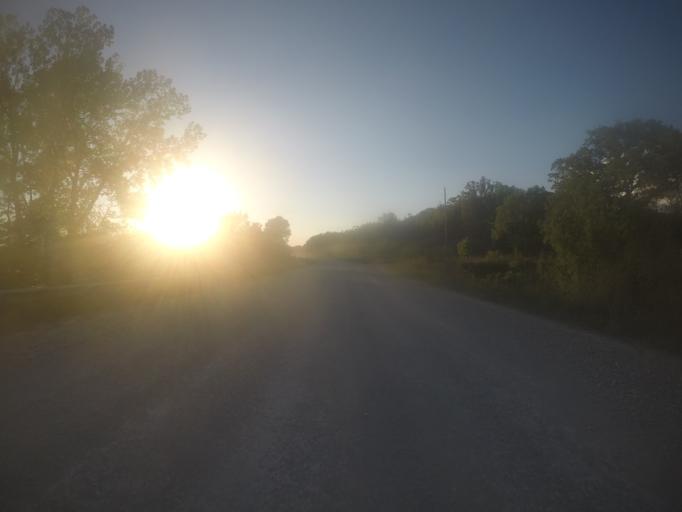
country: US
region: Kansas
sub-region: Riley County
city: Manhattan
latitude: 39.2410
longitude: -96.5604
